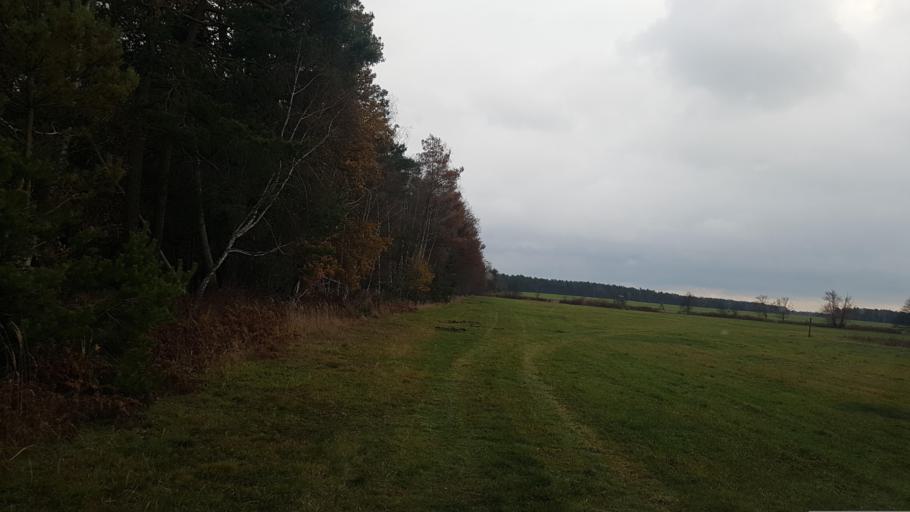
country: DE
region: Brandenburg
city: Ruckersdorf
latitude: 51.5614
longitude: 13.6070
